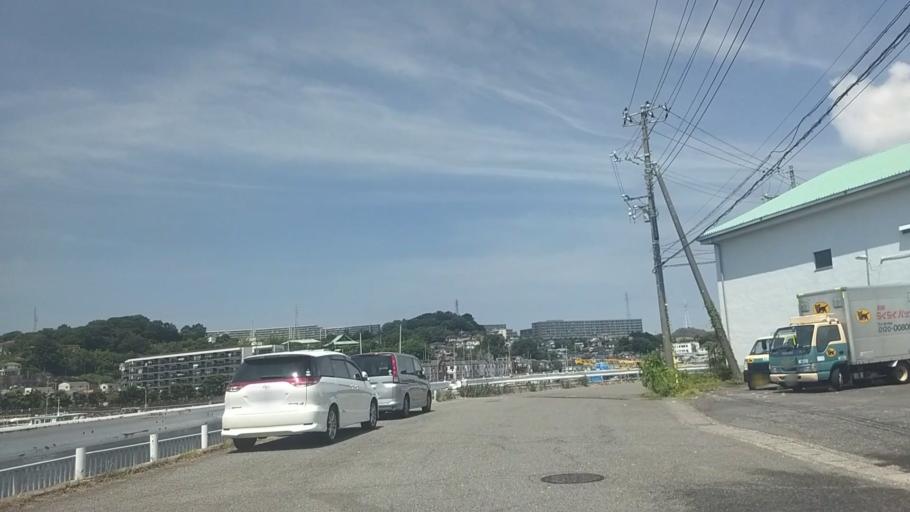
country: JP
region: Kanagawa
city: Yokosuka
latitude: 35.3085
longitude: 139.6405
